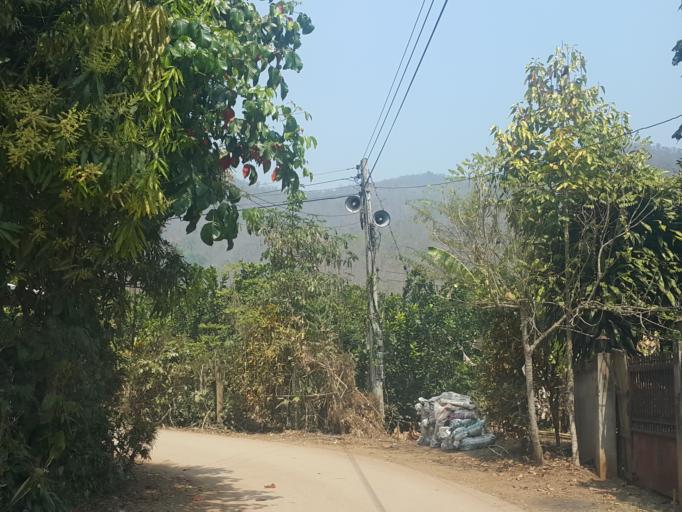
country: TH
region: Chiang Mai
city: Hang Dong
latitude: 18.7502
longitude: 98.8271
